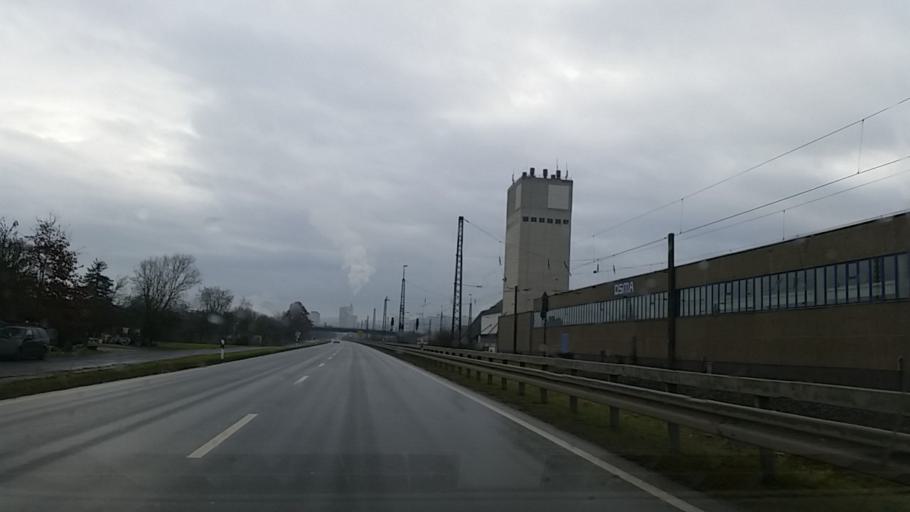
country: DE
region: Bavaria
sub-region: Regierungsbezirk Unterfranken
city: Karlstadt
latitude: 49.9704
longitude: 9.7681
